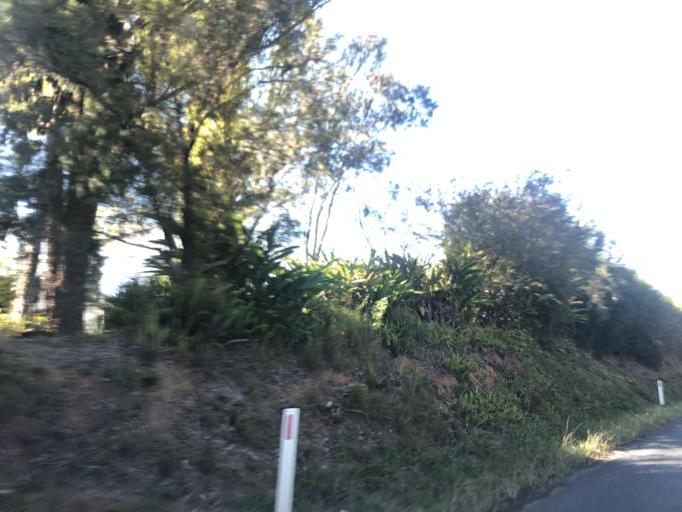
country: AU
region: New South Wales
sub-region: Coffs Harbour
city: Toormina
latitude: -30.3466
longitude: 153.0858
